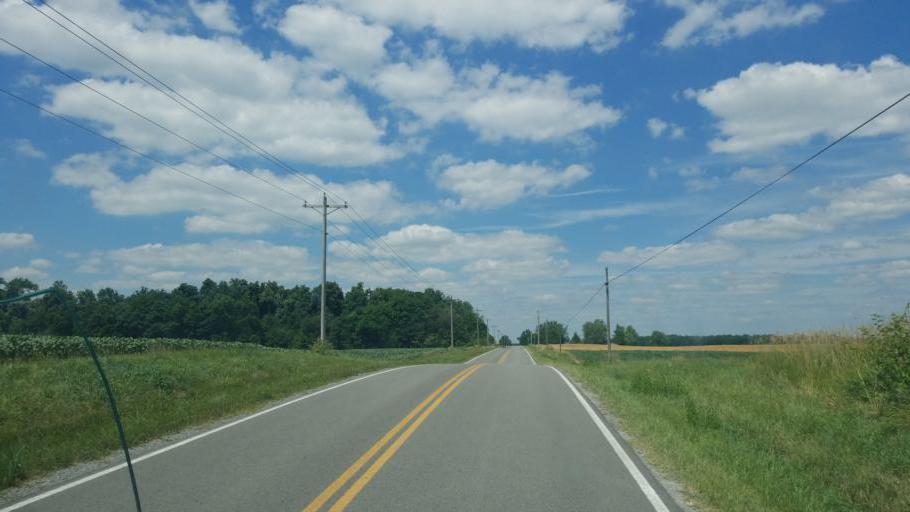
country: US
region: Ohio
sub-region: Williams County
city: Edgerton
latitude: 41.4191
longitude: -84.7101
